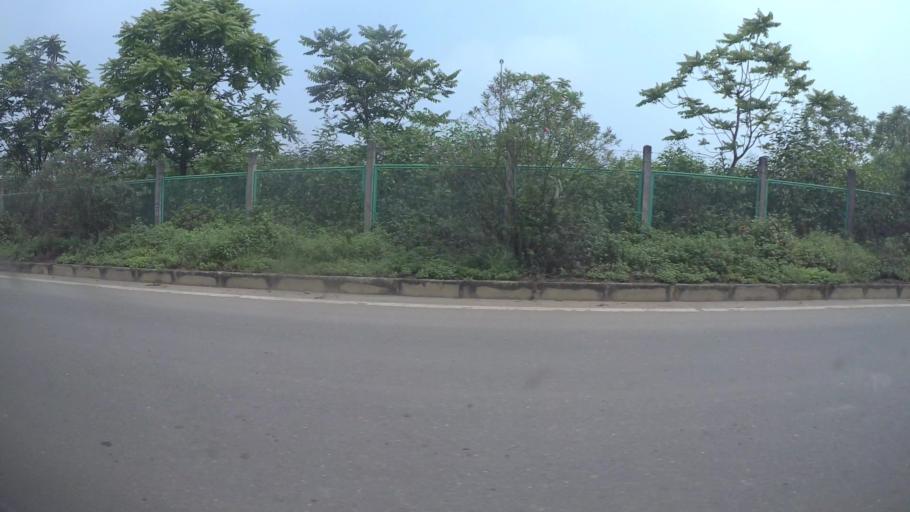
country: VN
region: Ha Noi
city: Lien Quan
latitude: 20.9887
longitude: 105.5675
